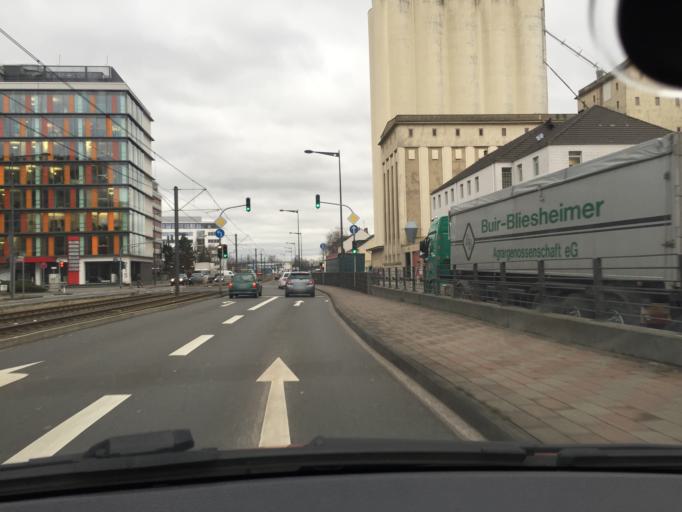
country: DE
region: North Rhine-Westphalia
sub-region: Regierungsbezirk Koln
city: Deutz
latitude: 50.9262
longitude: 6.9774
